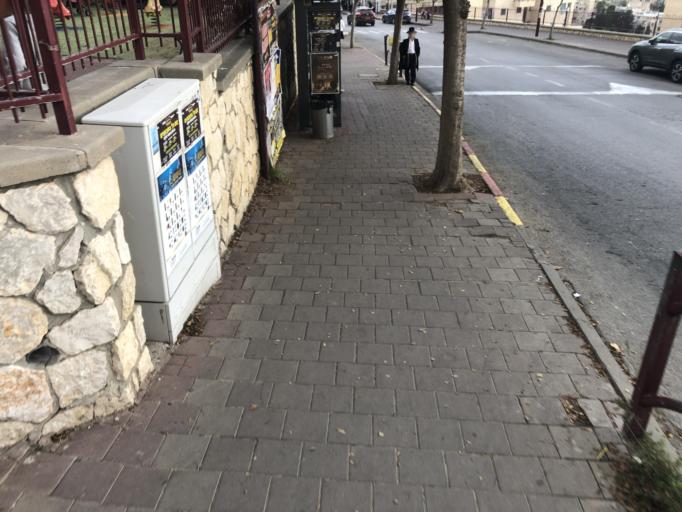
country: IL
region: Jerusalem
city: Modiin Ilit
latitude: 31.9376
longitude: 35.0387
